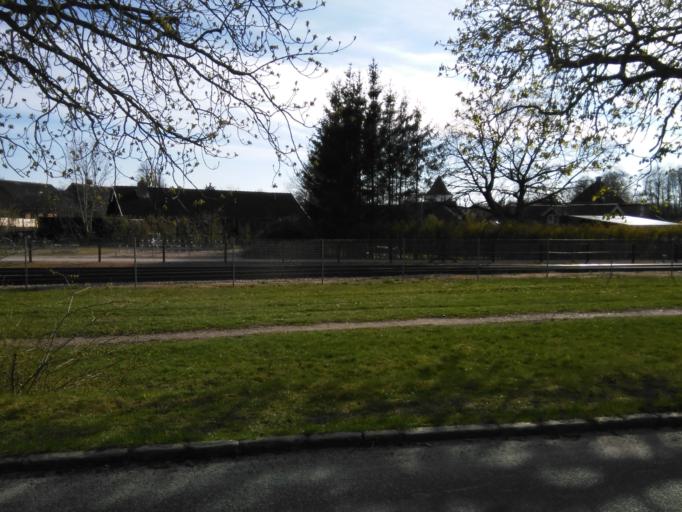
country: DK
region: Central Jutland
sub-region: Arhus Kommune
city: Marslet
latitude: 56.0691
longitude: 10.1638
